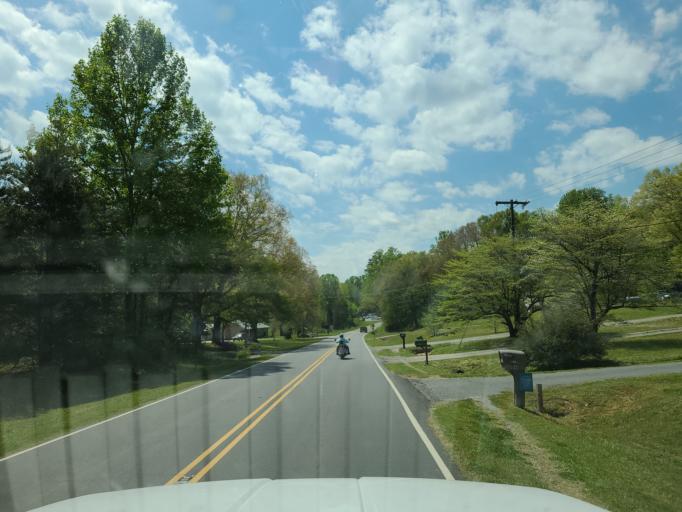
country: US
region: North Carolina
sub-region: Lincoln County
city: Lincolnton
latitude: 35.4487
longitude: -81.2779
